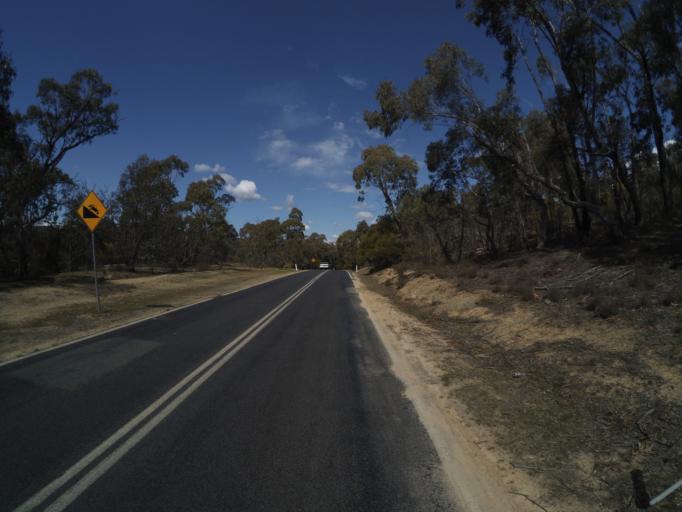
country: AU
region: Australian Capital Territory
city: Macquarie
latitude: -35.3573
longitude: 148.9455
